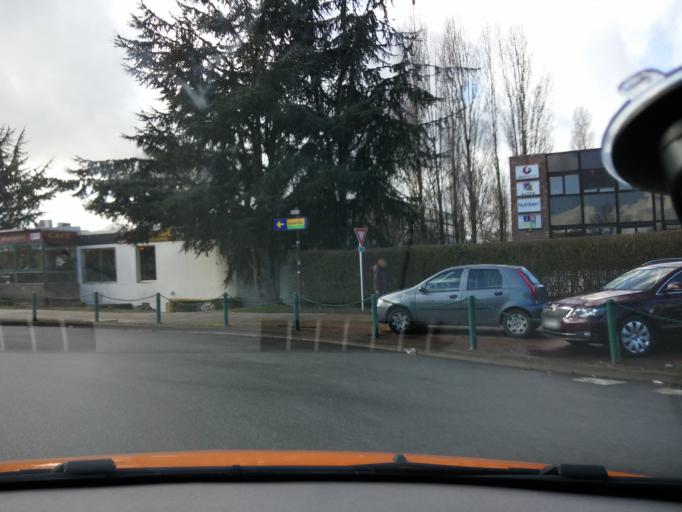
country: FR
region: Ile-de-France
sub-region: Departement de l'Essonne
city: Orsay
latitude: 48.6857
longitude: 2.2059
